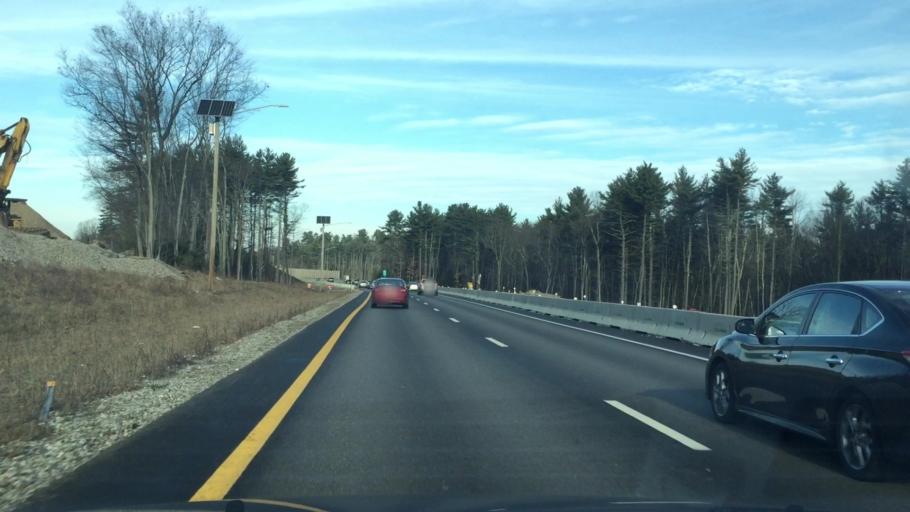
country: US
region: New Hampshire
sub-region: Rockingham County
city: Auburn
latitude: 42.9399
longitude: -71.3853
